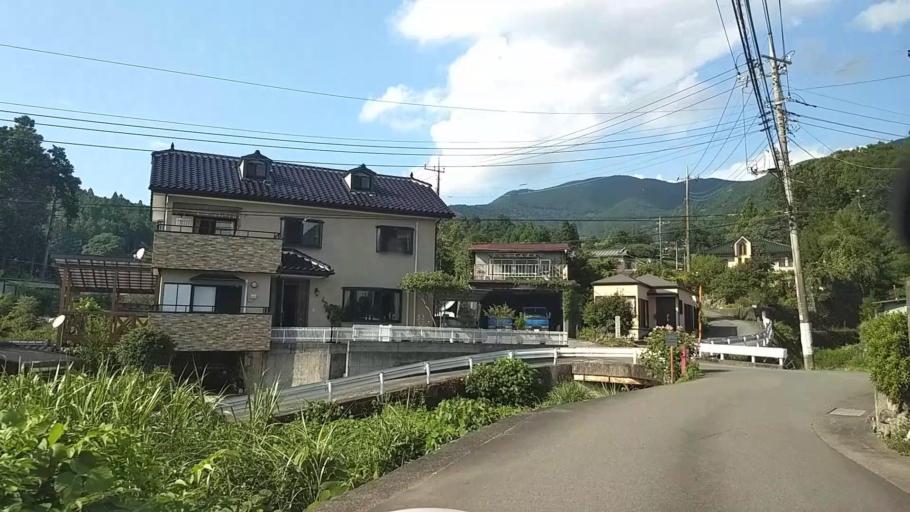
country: JP
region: Shizuoka
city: Fujinomiya
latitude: 35.2830
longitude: 138.4659
